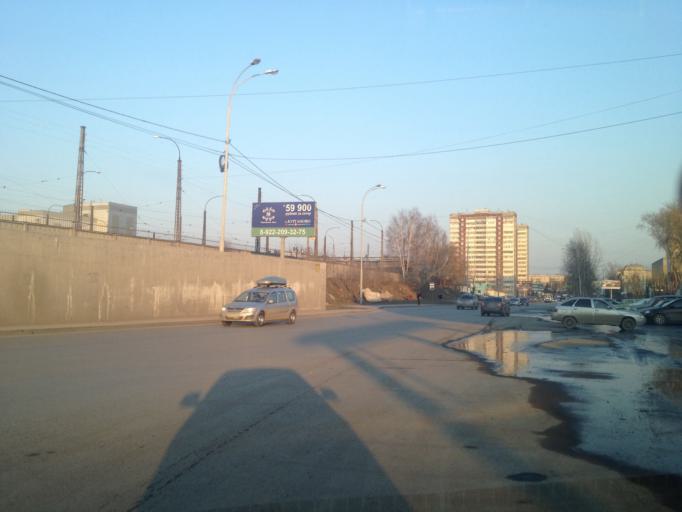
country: RU
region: Sverdlovsk
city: Sovkhoznyy
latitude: 56.8117
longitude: 60.5420
